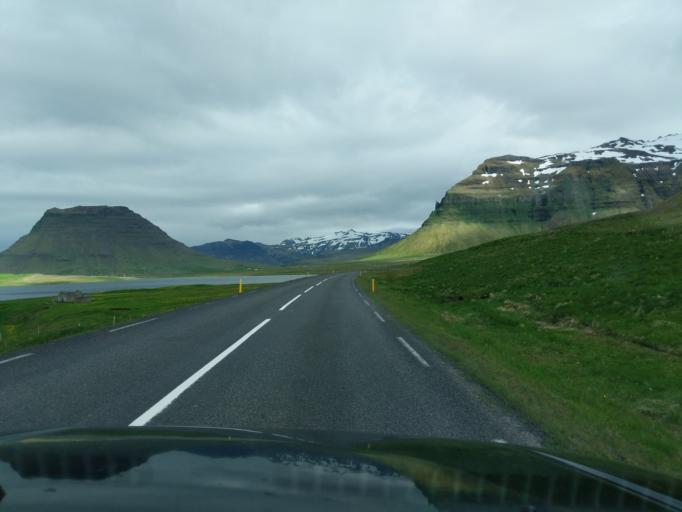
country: IS
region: West
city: Olafsvik
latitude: 64.9431
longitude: -23.3887
